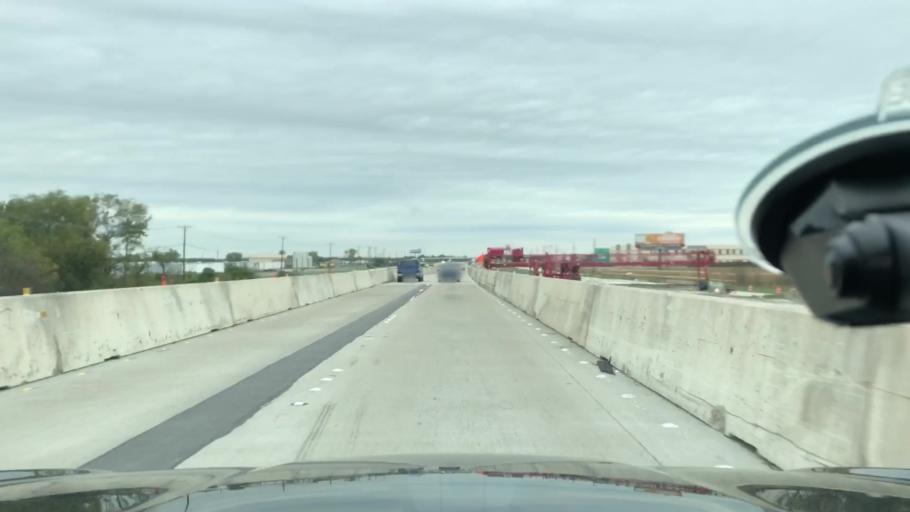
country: US
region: Texas
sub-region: Ellis County
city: Waxahachie
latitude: 32.4496
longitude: -96.8473
